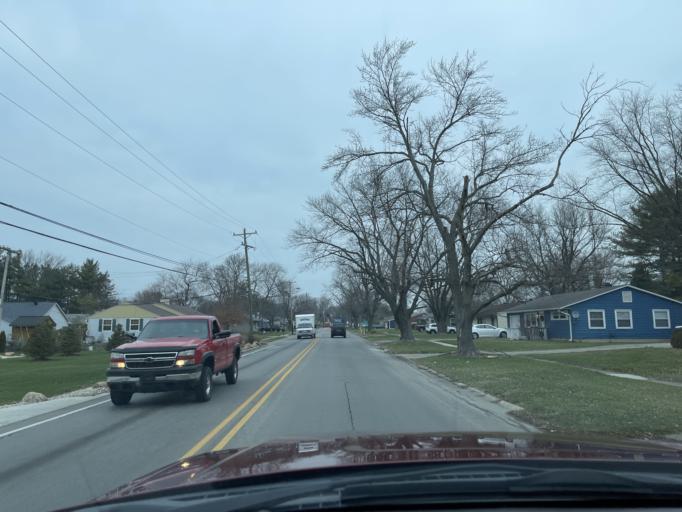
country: US
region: Indiana
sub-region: Hendricks County
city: Brownsburg
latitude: 39.8337
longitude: -86.4012
